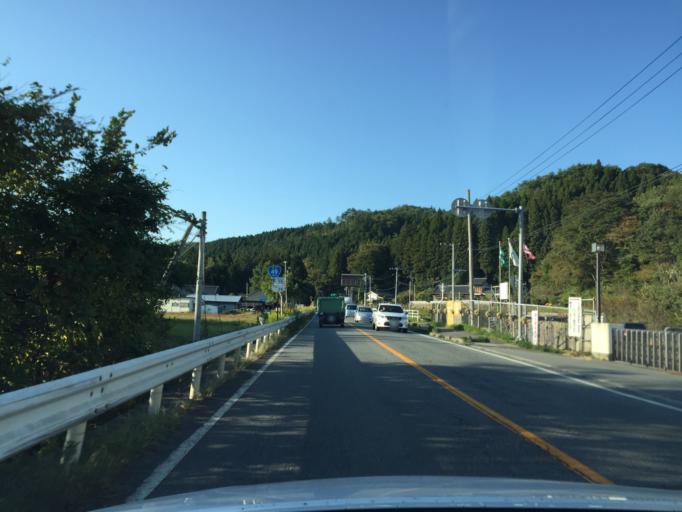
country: JP
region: Fukushima
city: Iwaki
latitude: 37.1057
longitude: 140.7707
